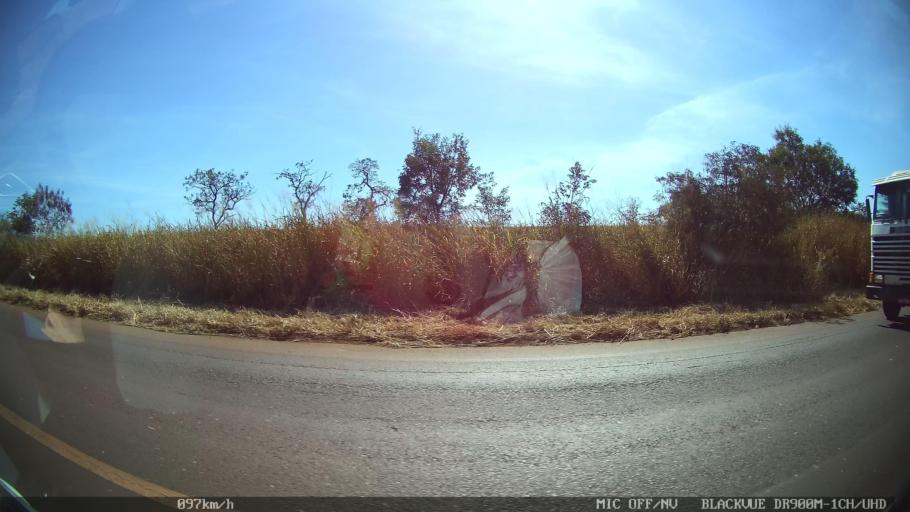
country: BR
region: Sao Paulo
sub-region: Barretos
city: Barretos
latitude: -20.4598
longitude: -48.4654
